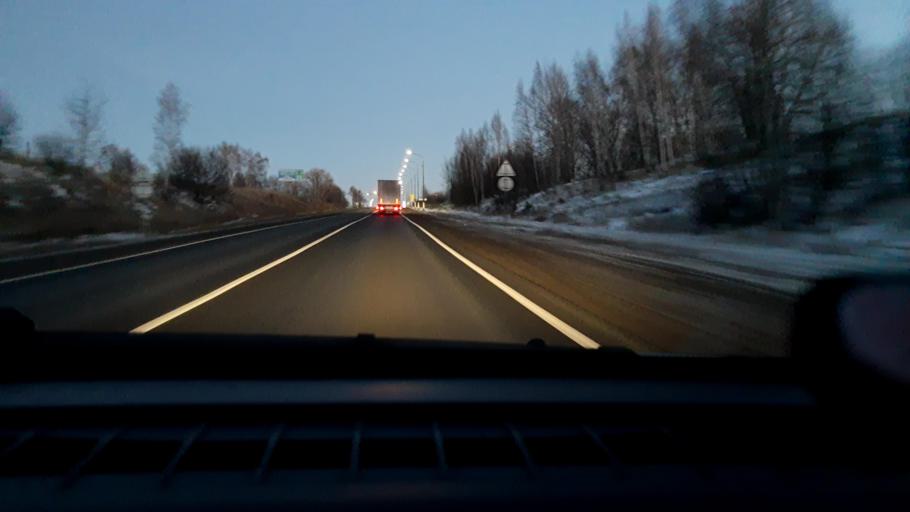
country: RU
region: Nizjnij Novgorod
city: Lyskovo
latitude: 56.0162
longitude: 45.0032
